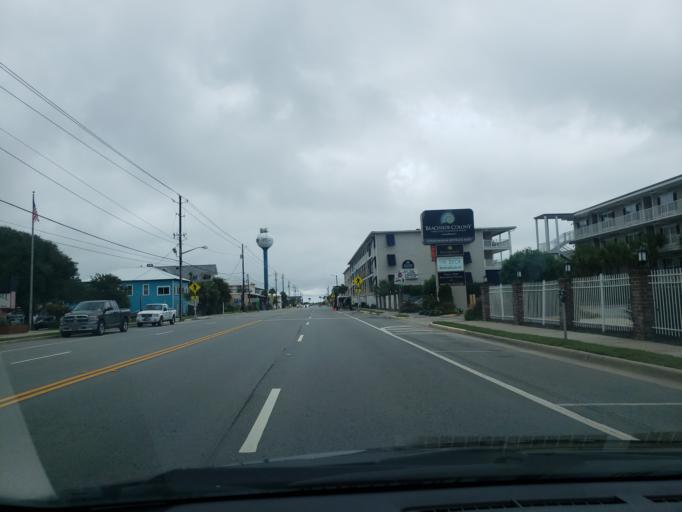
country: US
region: Georgia
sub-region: Chatham County
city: Tybee Island
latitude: 32.0083
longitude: -80.8428
